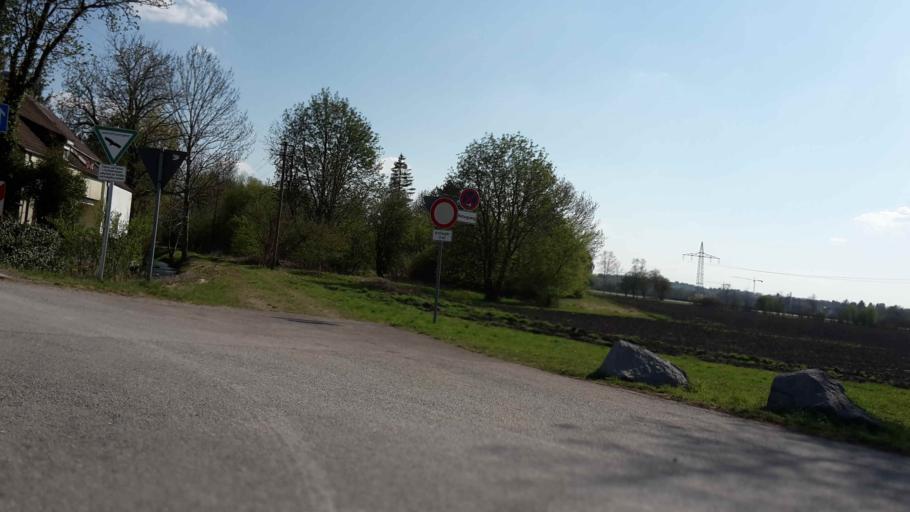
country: DE
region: Bavaria
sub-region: Upper Bavaria
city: Karlsfeld
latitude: 48.1920
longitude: 11.4216
